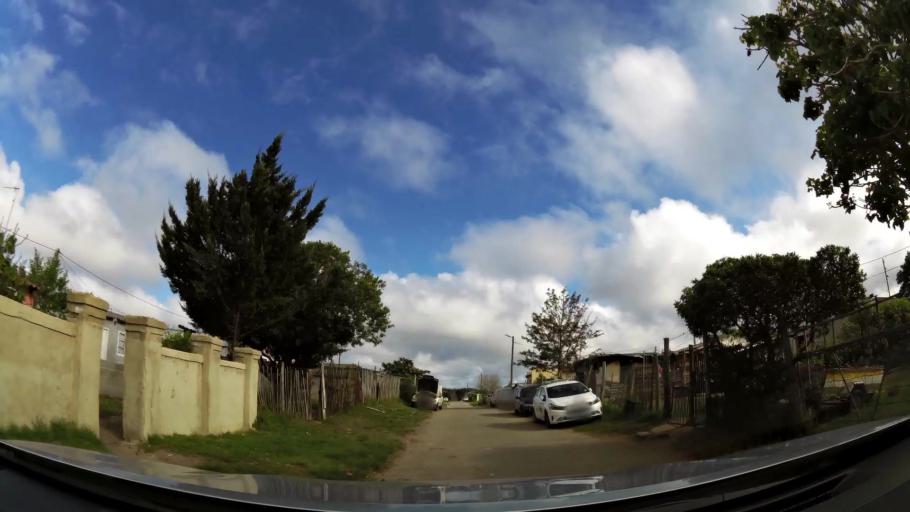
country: ZA
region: Western Cape
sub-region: Eden District Municipality
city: Plettenberg Bay
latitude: -34.0490
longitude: 23.3266
